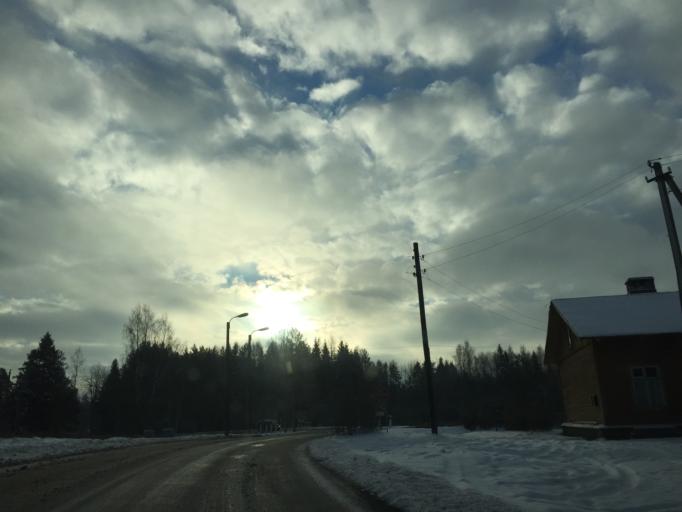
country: LV
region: Amatas Novads
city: Drabesi
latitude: 57.2270
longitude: 25.2805
